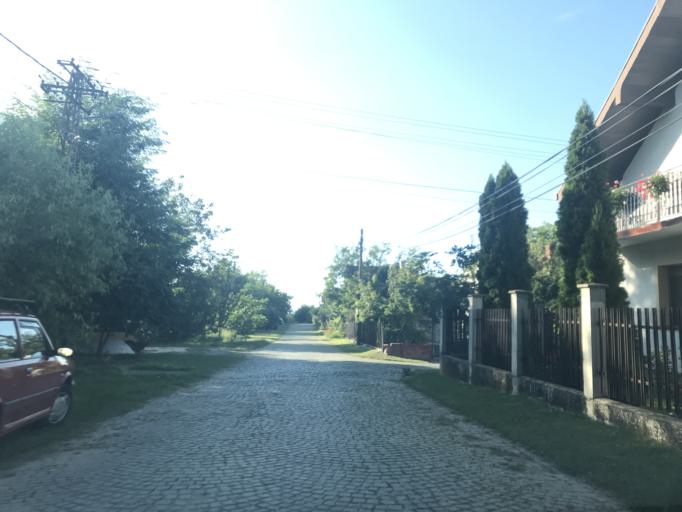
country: RS
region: Autonomna Pokrajina Vojvodina
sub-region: Juznobacki Okrug
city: Novi Sad
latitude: 45.2084
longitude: 19.8007
